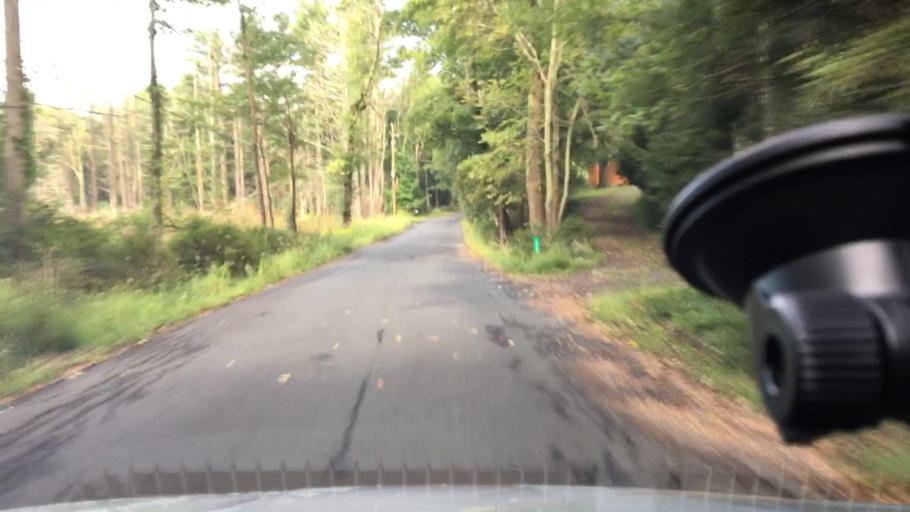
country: US
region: Pennsylvania
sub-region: Monroe County
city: Mountainhome
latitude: 41.1623
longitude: -75.2640
